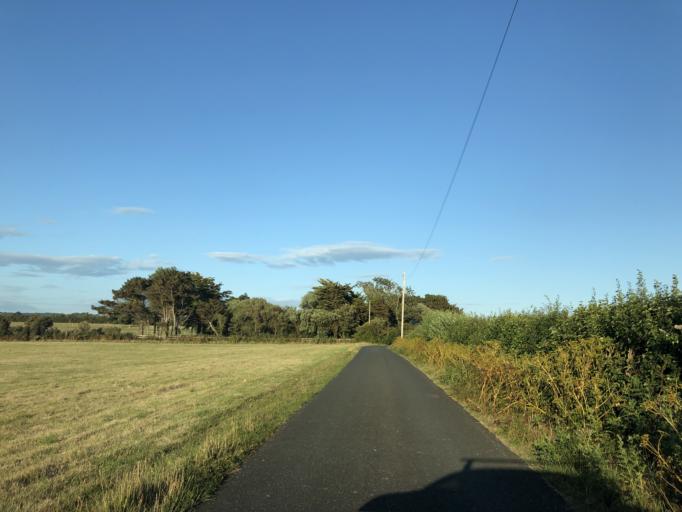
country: GB
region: England
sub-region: Isle of Wight
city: Chale
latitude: 50.6301
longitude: -1.3754
